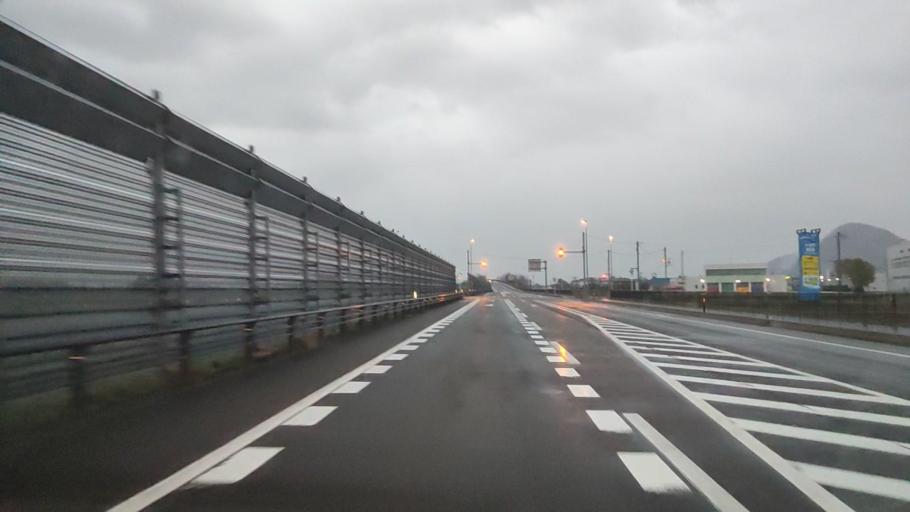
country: JP
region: Akita
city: Omagari
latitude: 39.5023
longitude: 140.4100
